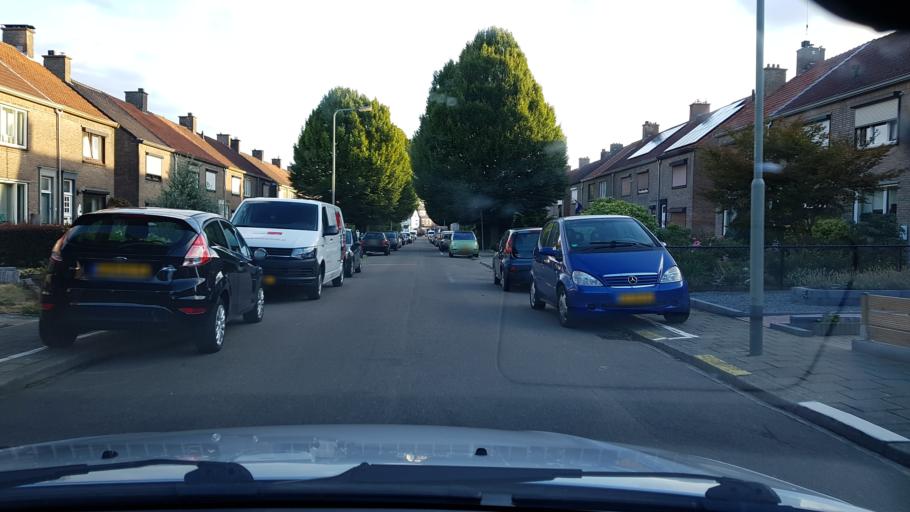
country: NL
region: Limburg
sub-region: Gemeente Sittard-Geleen
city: Limbricht
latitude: 50.9722
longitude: 5.8378
